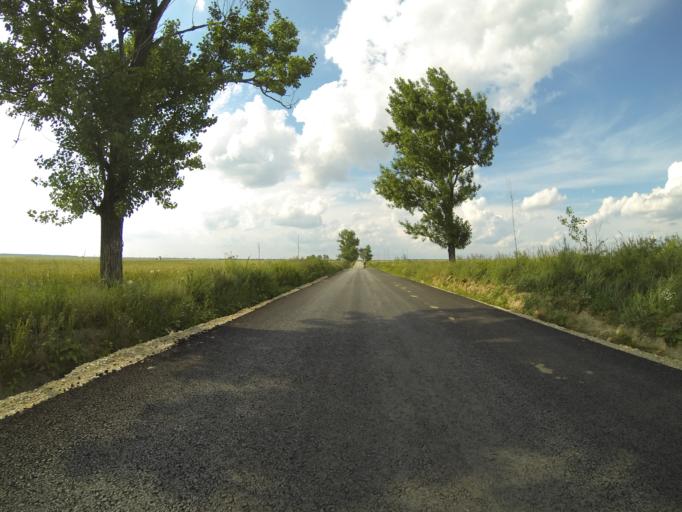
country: RO
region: Dolj
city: Satu Nou Calopar
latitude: 44.1393
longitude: 23.7948
